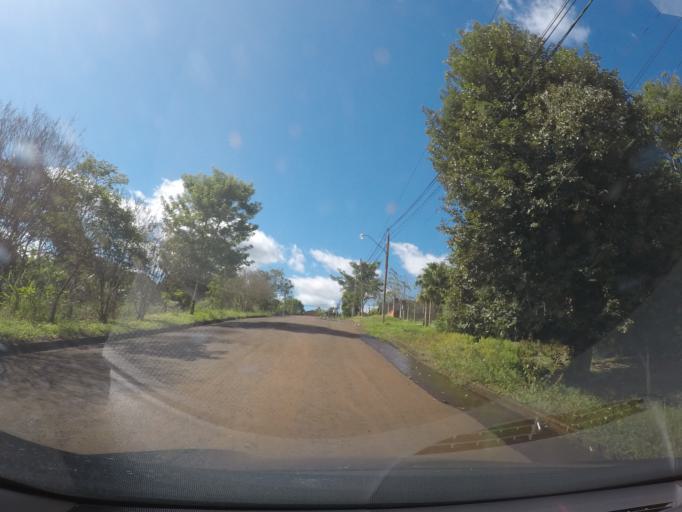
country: AR
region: Misiones
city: Puerto Rico
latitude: -26.7974
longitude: -55.0149
